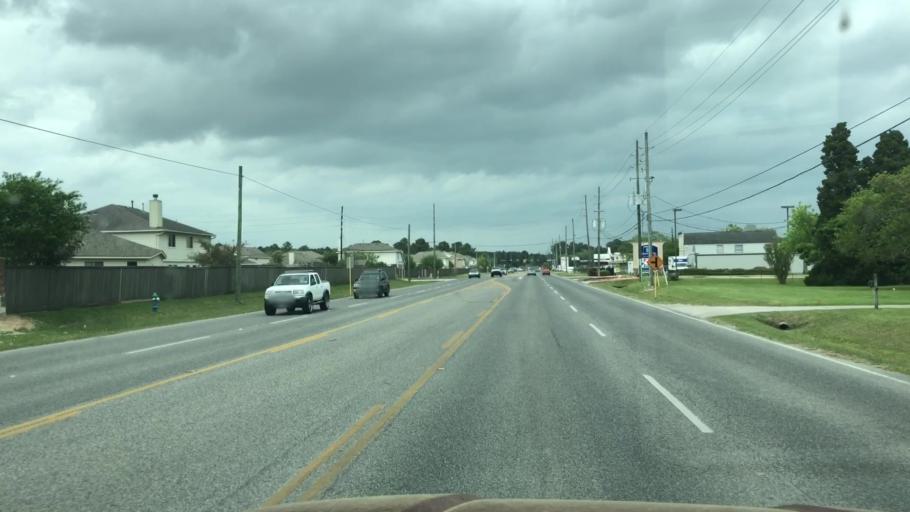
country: US
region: Texas
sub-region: Harris County
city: Spring
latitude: 30.0537
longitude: -95.4941
